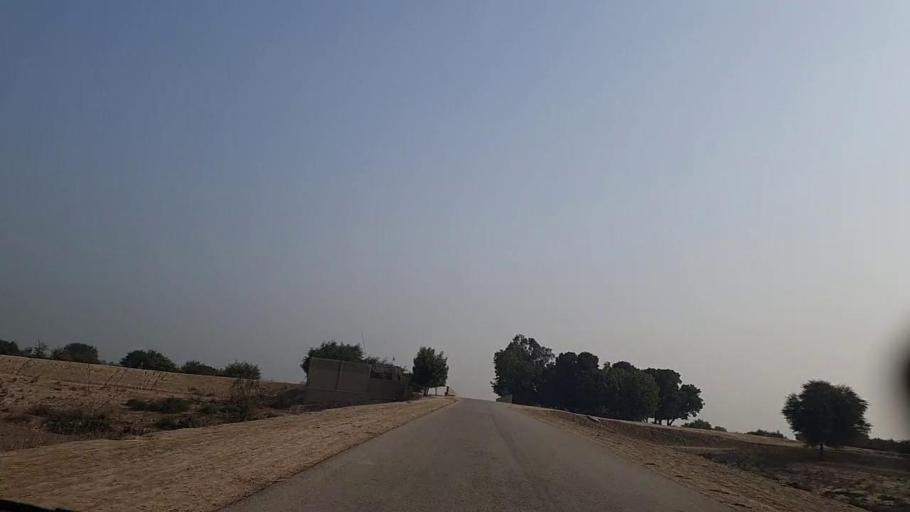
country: PK
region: Sindh
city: Sann
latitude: 26.1697
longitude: 68.1082
